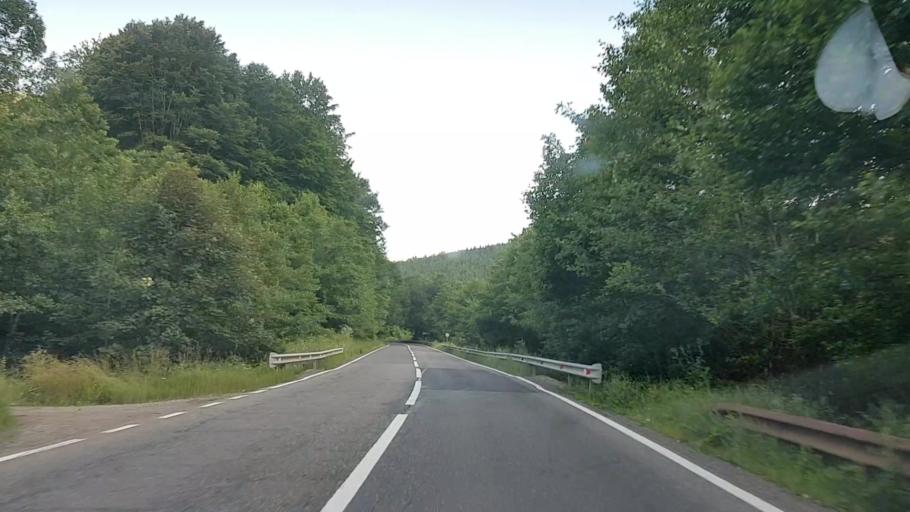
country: RO
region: Harghita
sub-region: Comuna Corund
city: Corund
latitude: 46.4563
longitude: 25.2106
